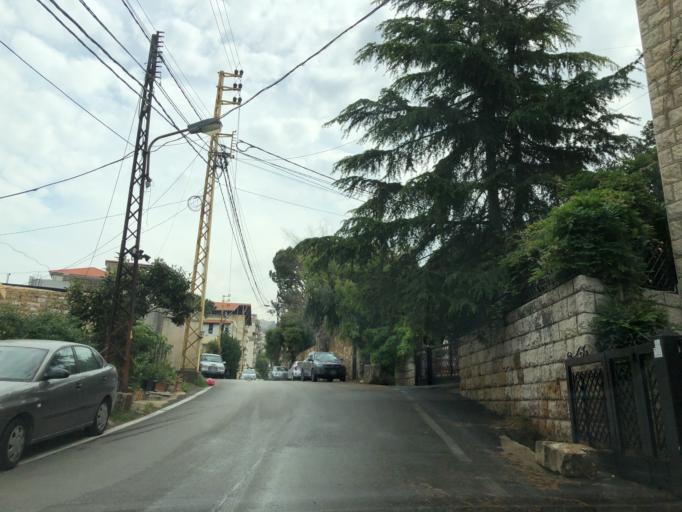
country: LB
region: Mont-Liban
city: Jdaidet el Matn
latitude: 33.8590
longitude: 35.5925
